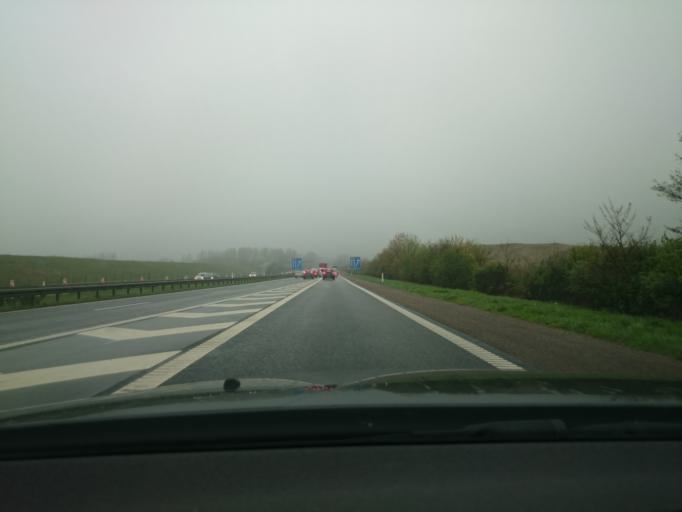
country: DK
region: Capital Region
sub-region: Ballerup Kommune
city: Ballerup
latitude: 55.7072
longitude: 12.3679
